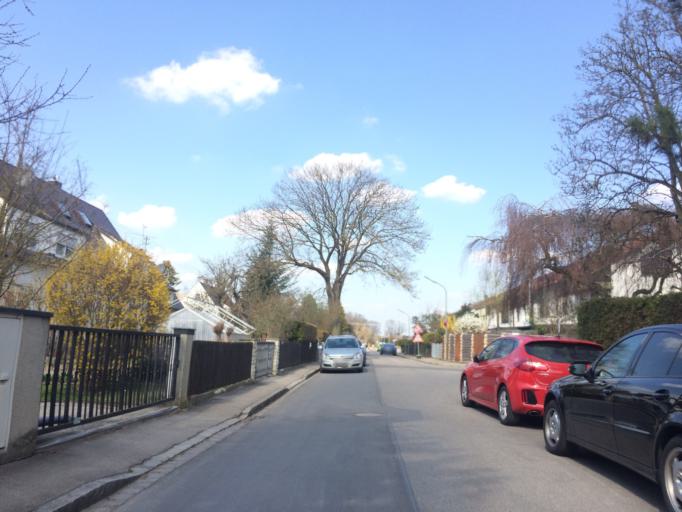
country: DE
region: Bavaria
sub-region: Swabia
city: Gersthofen
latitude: 48.4085
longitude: 10.8968
